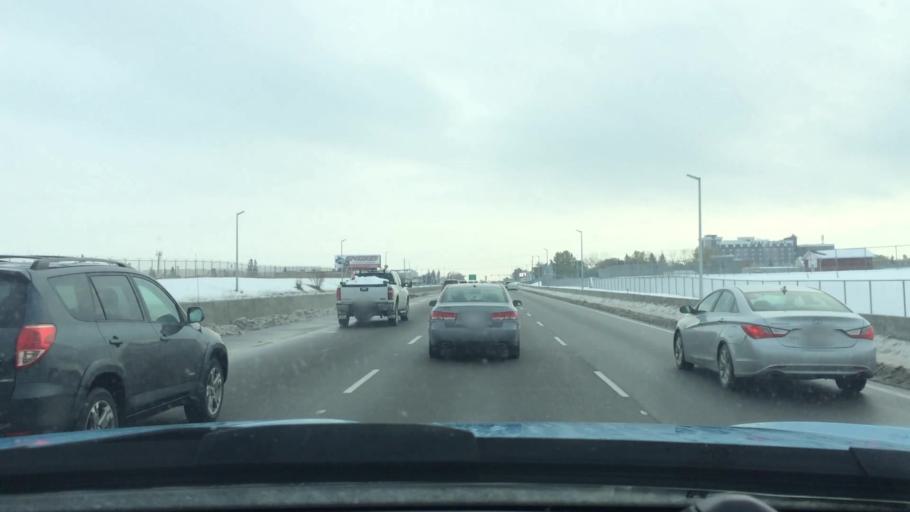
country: CA
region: Alberta
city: Calgary
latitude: 51.0927
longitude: -114.0199
